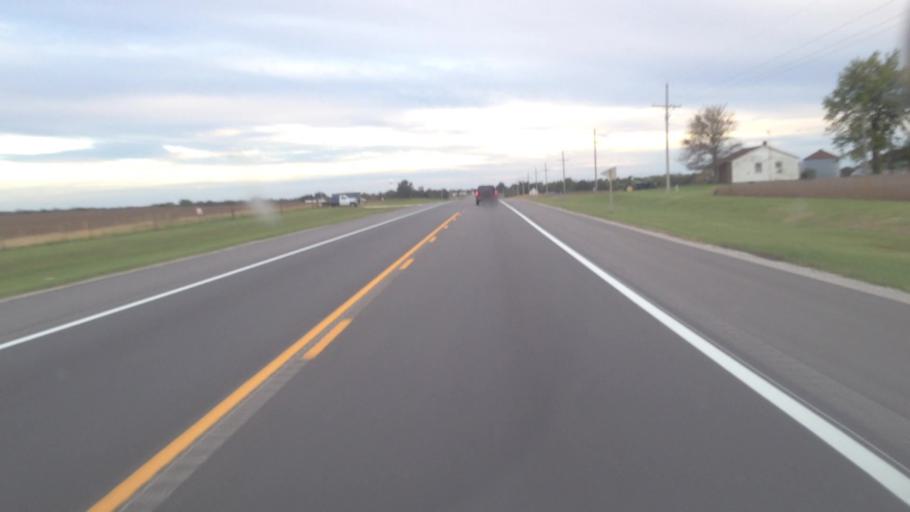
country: US
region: Kansas
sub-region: Franklin County
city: Ottawa
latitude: 38.5060
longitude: -95.2675
